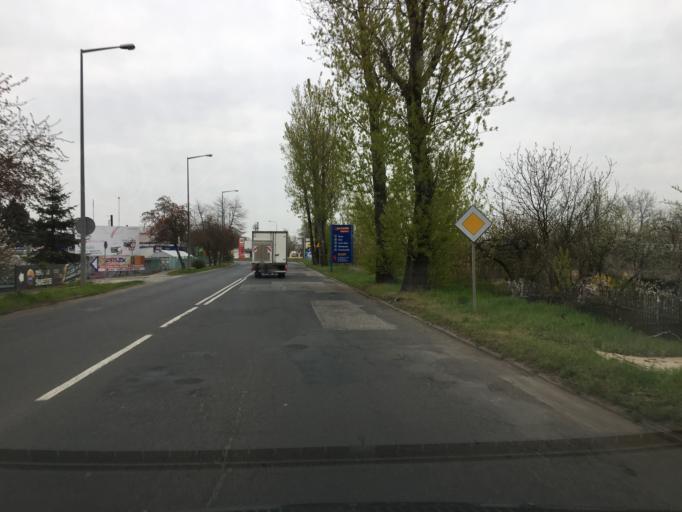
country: PL
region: Lower Silesian Voivodeship
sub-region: Legnica
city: Legnica
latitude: 51.1892
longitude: 16.1728
